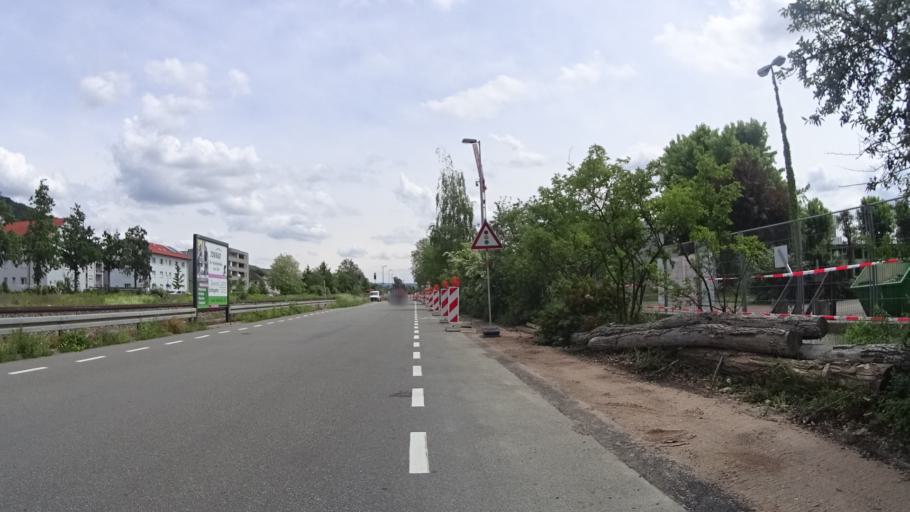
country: CH
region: Basel-City
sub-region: Basel-Stadt
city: Bettingen
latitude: 47.5503
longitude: 7.6626
